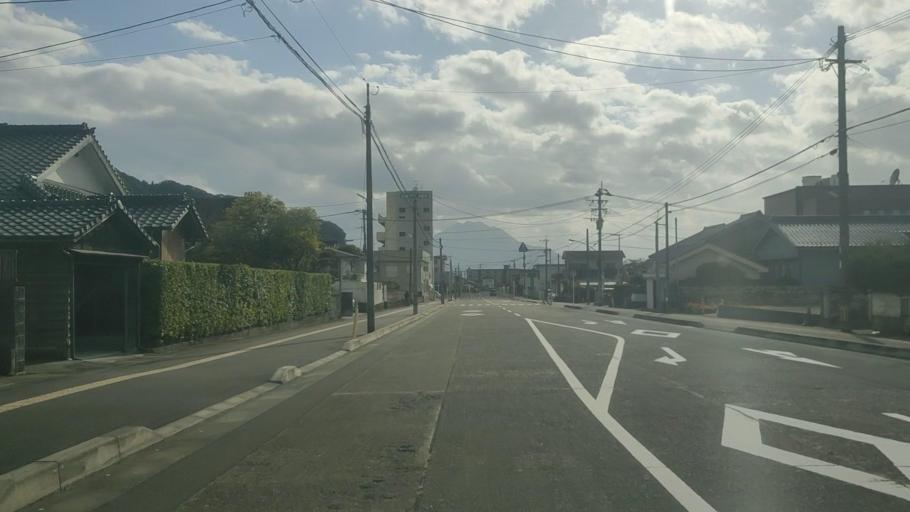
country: JP
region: Kagoshima
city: Kajiki
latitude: 31.7384
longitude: 130.6704
